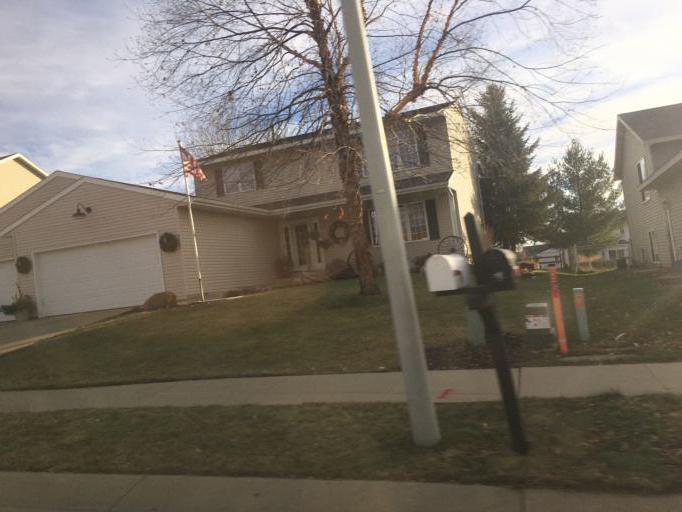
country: US
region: Minnesota
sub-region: Olmsted County
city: Oronoco
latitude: 44.0862
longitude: -92.5329
